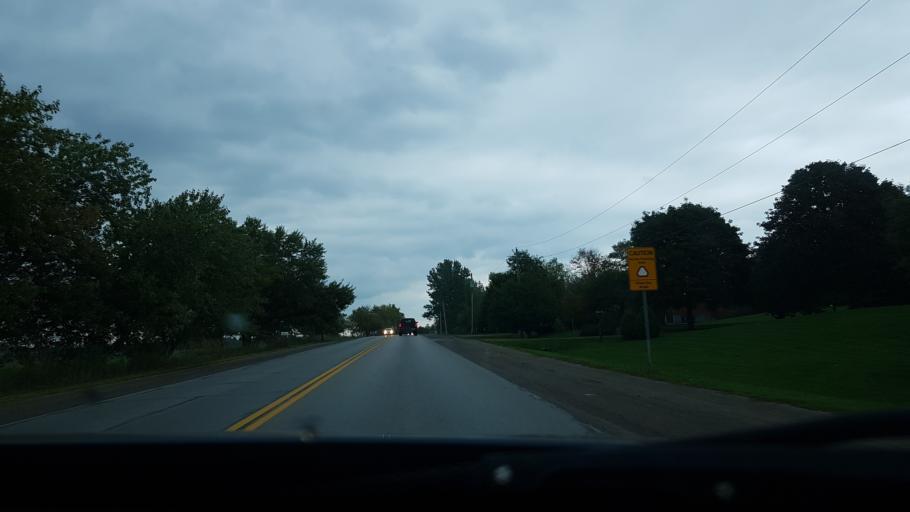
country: CA
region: Ontario
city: Omemee
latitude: 44.3622
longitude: -78.7167
